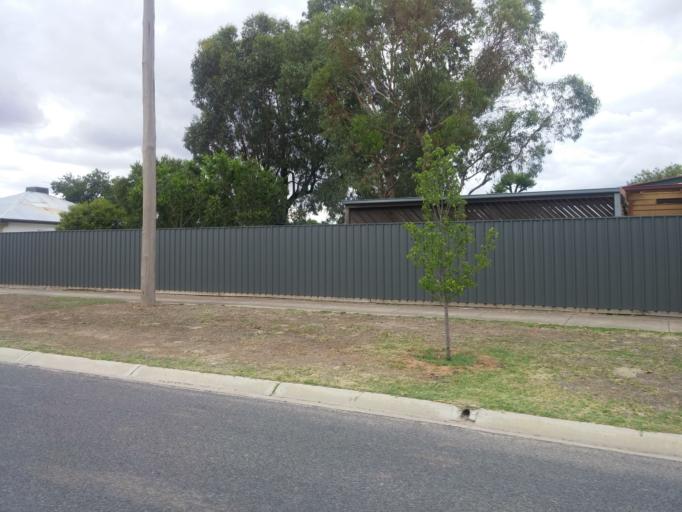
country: AU
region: Victoria
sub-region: Horsham
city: Horsham
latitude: -36.7258
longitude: 142.2024
